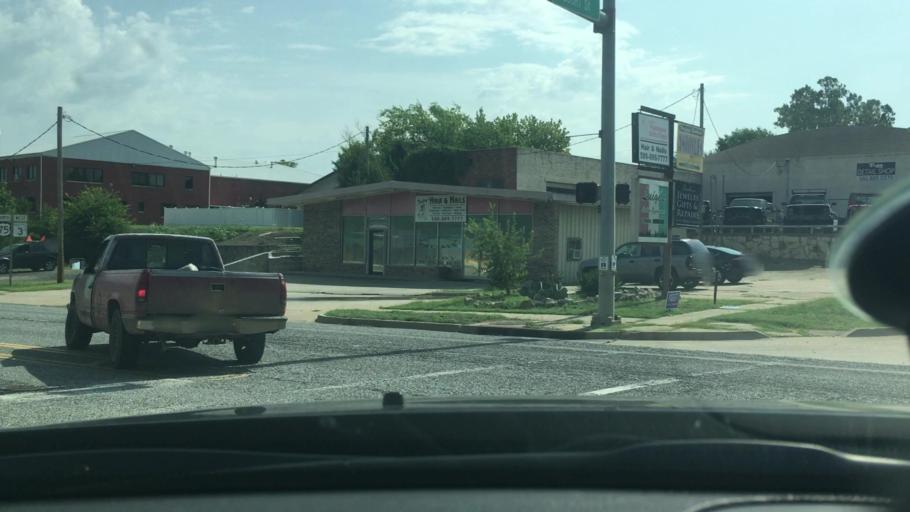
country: US
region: Oklahoma
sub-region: Atoka County
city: Atoka
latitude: 34.3862
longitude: -96.1282
